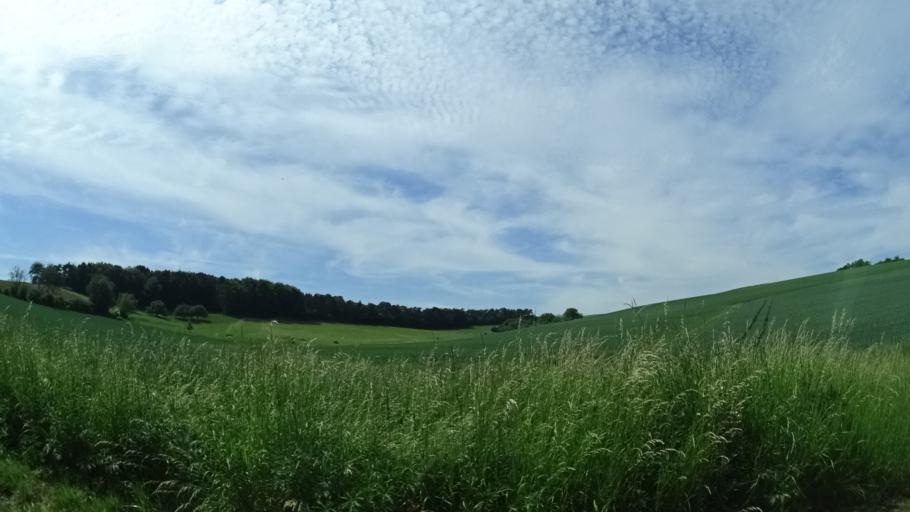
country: DE
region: Bavaria
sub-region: Regierungsbezirk Unterfranken
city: Birkenfeld
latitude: 49.8670
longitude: 9.7136
